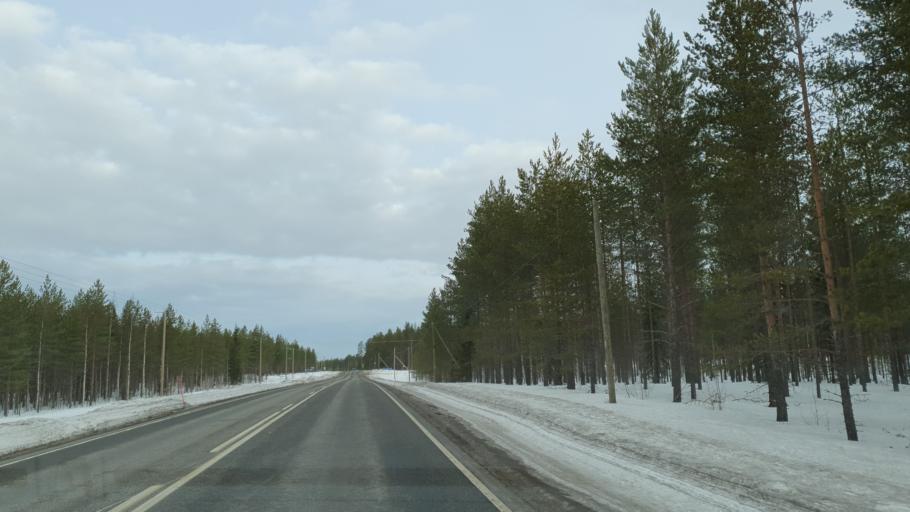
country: FI
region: Kainuu
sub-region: Kajaani
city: Vuokatti
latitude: 64.2135
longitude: 28.1326
